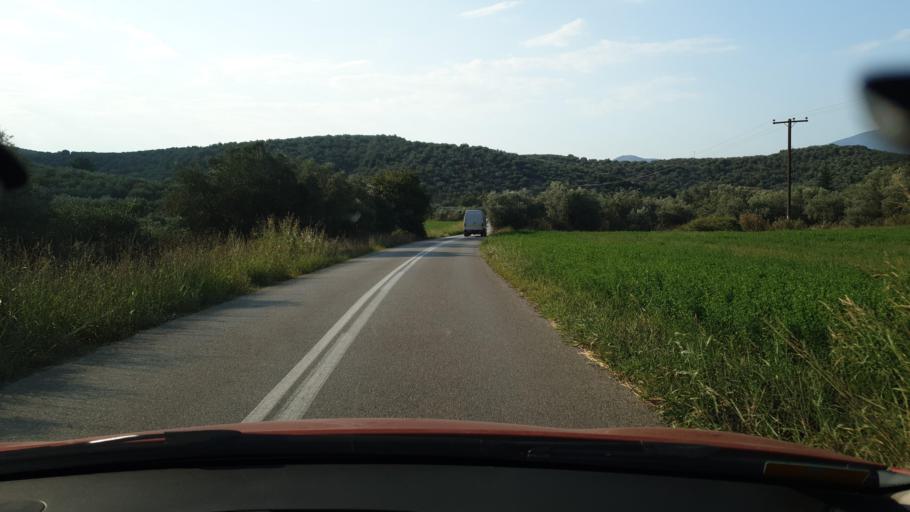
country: GR
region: Thessaly
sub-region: Nomos Magnisias
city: Pteleos
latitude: 38.9932
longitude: 22.9615
